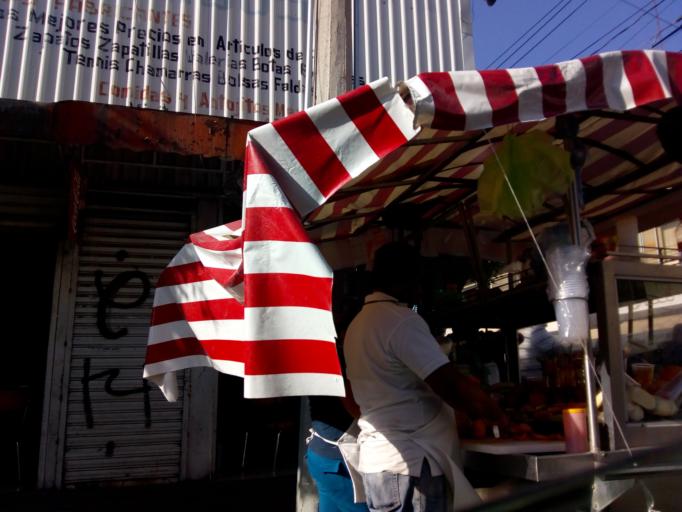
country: MX
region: Guanajuato
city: Leon
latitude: 21.1213
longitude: -101.6636
